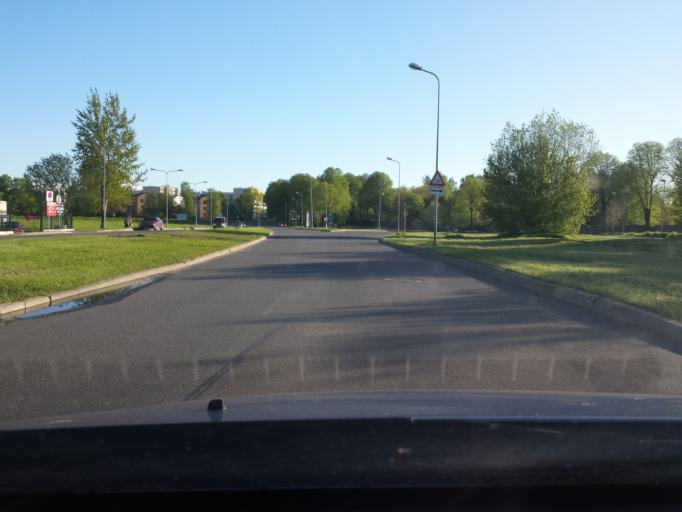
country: LV
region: Riga
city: Jaunciems
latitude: 56.9920
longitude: 24.1673
